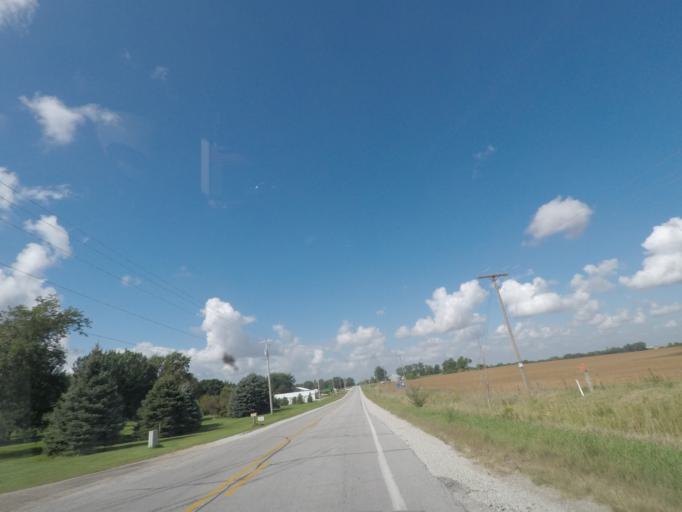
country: US
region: Iowa
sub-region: Story County
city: Nevada
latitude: 42.0225
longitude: -93.3126
